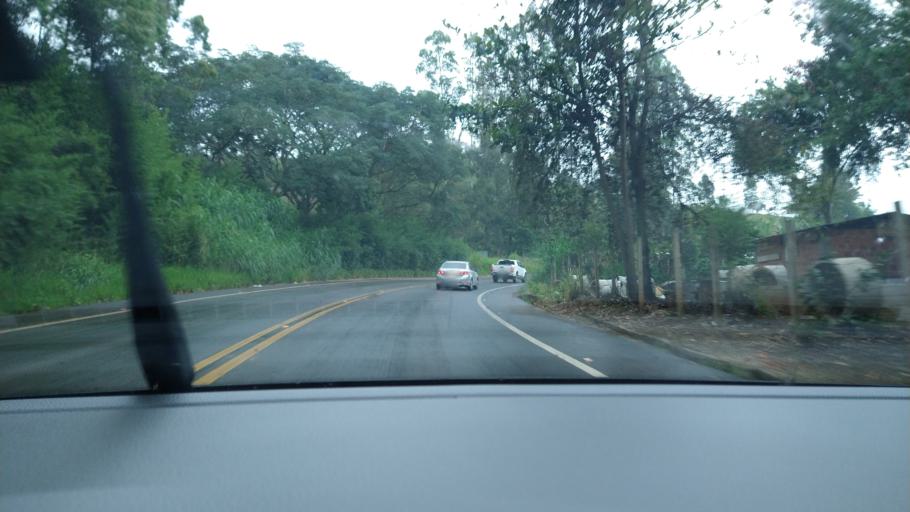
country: BR
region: Minas Gerais
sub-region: Vicosa
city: Vicosa
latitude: -20.6480
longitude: -42.8653
